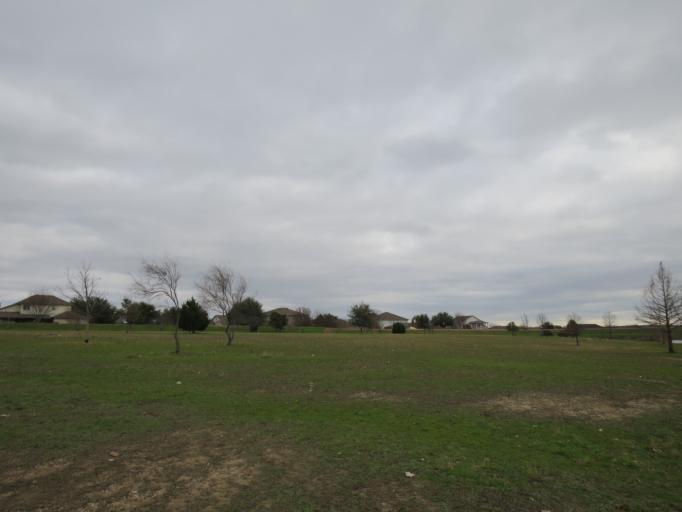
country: US
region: Texas
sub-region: Williamson County
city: Round Rock
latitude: 30.5389
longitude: -97.6252
